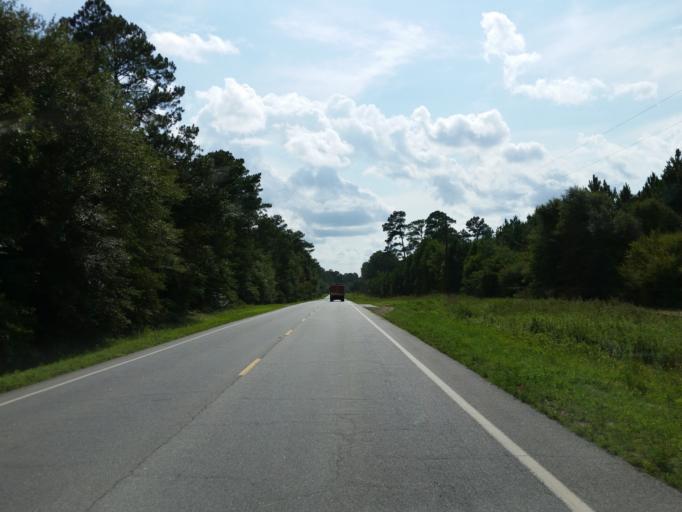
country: US
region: Georgia
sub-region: Lee County
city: Leesburg
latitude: 31.7253
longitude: -83.9973
